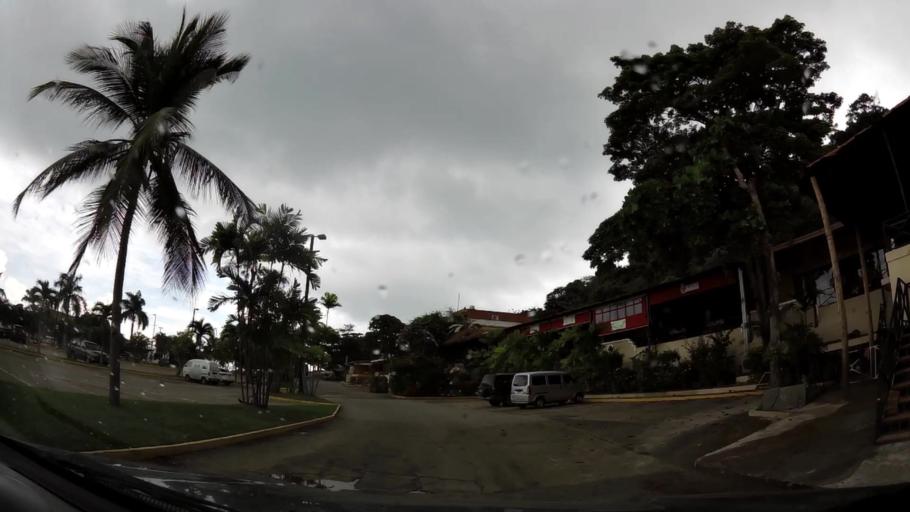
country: PA
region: Panama
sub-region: Distrito de Panama
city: Ancon
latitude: 8.9099
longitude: -79.5212
